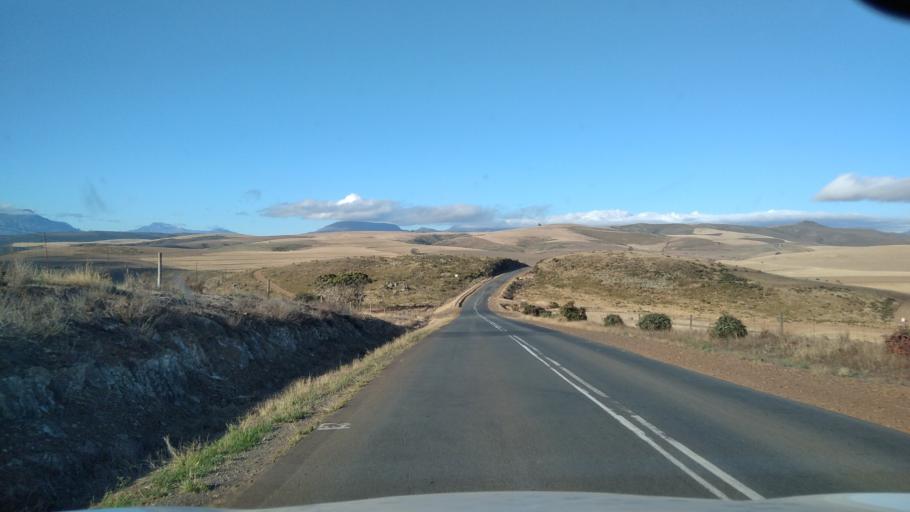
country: ZA
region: Western Cape
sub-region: Overberg District Municipality
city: Caledon
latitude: -34.1795
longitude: 19.2777
